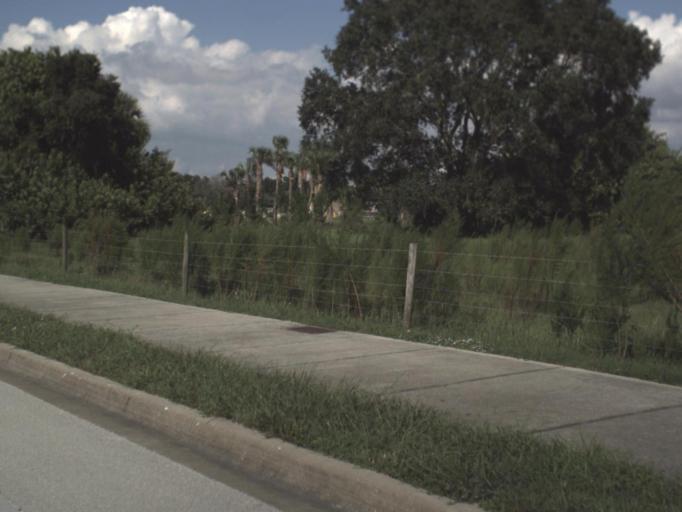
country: US
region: Florida
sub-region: Sarasota County
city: South Venice
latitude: 27.0314
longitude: -82.3978
